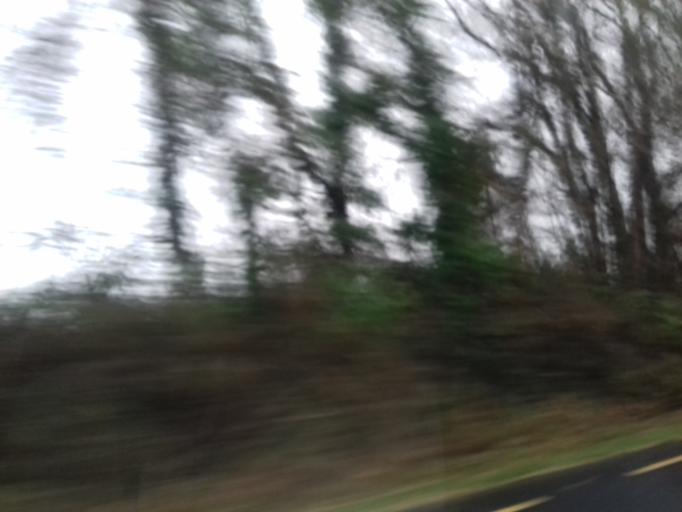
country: IE
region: Ulster
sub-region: County Monaghan
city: Castleblayney
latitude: 54.1081
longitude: -6.7183
